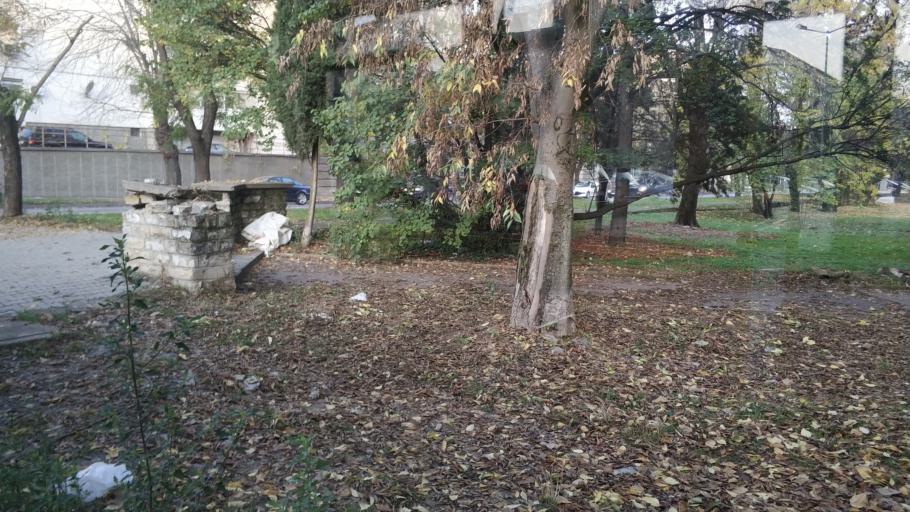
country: BG
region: Stara Zagora
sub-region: Obshtina Stara Zagora
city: Stara Zagora
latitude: 42.4188
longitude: 25.6266
